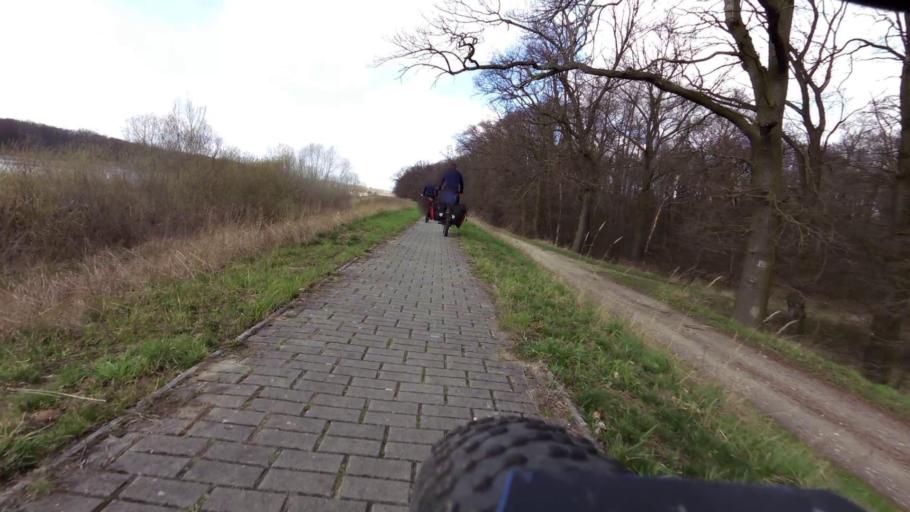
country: PL
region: Lubusz
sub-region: Powiat slubicki
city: Slubice
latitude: 52.3851
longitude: 14.5461
